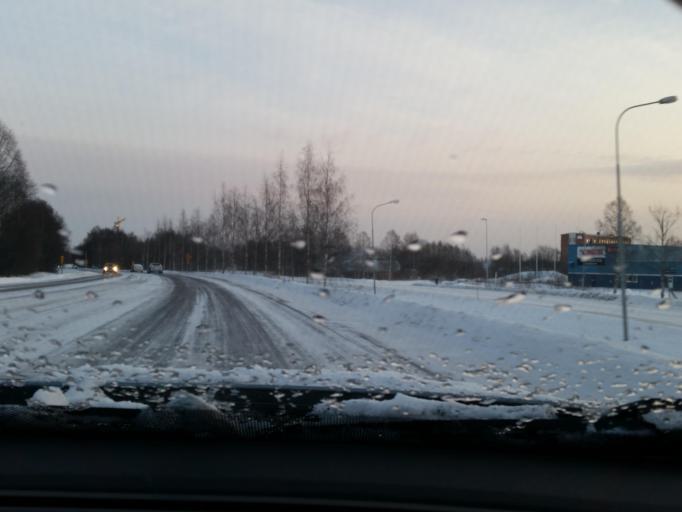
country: SE
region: Norrbotten
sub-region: Pitea Kommun
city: Pitea
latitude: 65.3169
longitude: 21.4500
